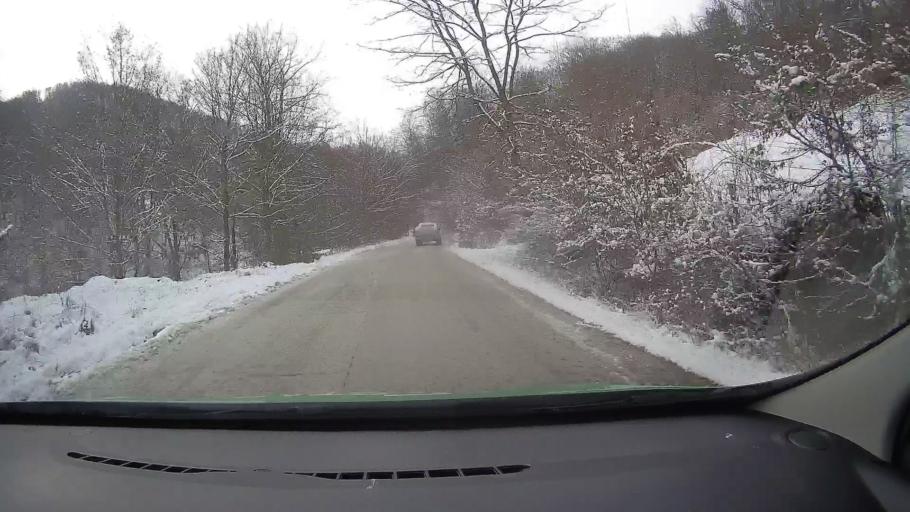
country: RO
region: Alba
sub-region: Oras Zlatna
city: Zlatna
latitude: 46.0977
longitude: 23.1829
